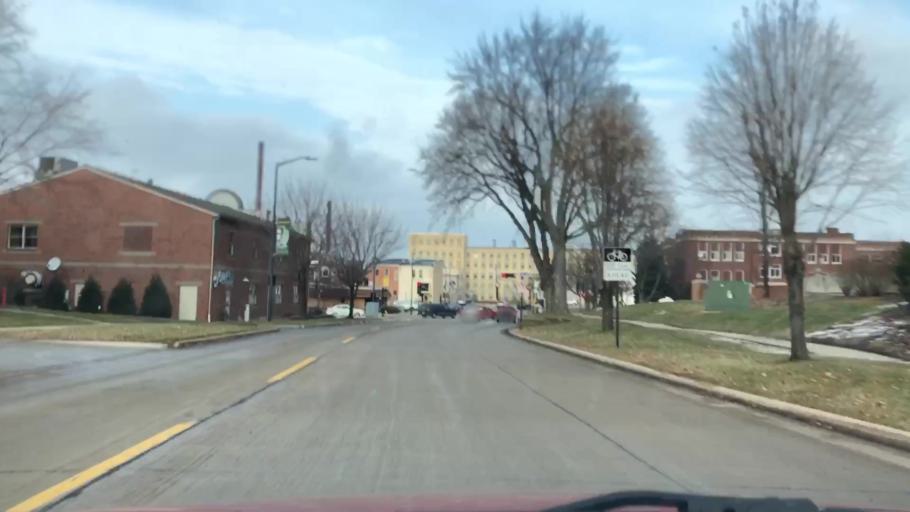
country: US
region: Wisconsin
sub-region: Brown County
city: De Pere
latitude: 44.4455
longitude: -88.0686
